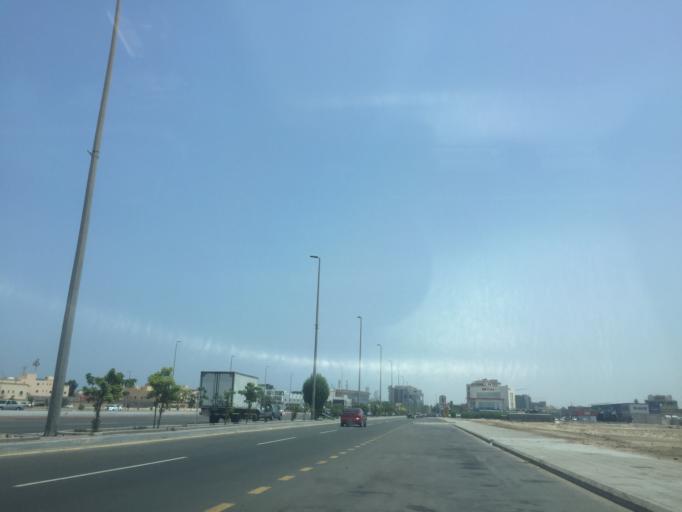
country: SA
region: Makkah
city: Jeddah
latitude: 21.5942
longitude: 39.1234
